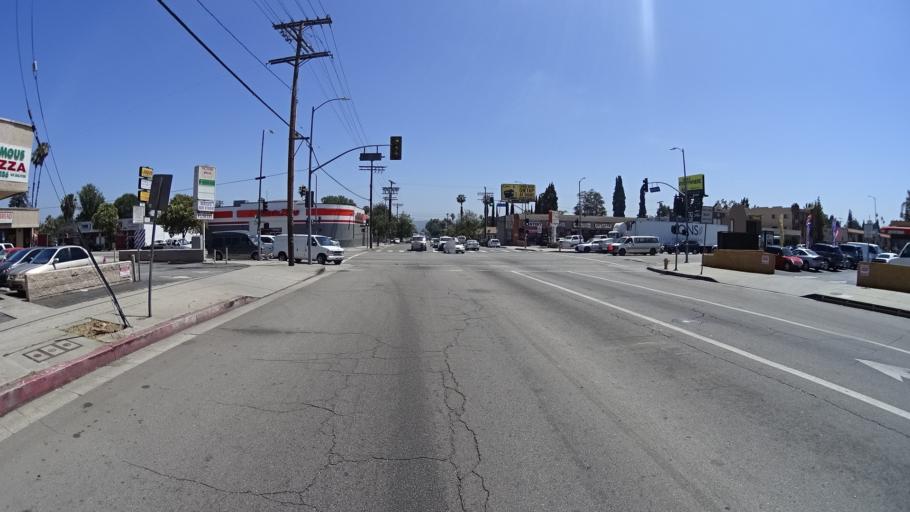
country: US
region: California
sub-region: Los Angeles County
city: Van Nuys
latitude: 34.1870
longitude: -118.4399
